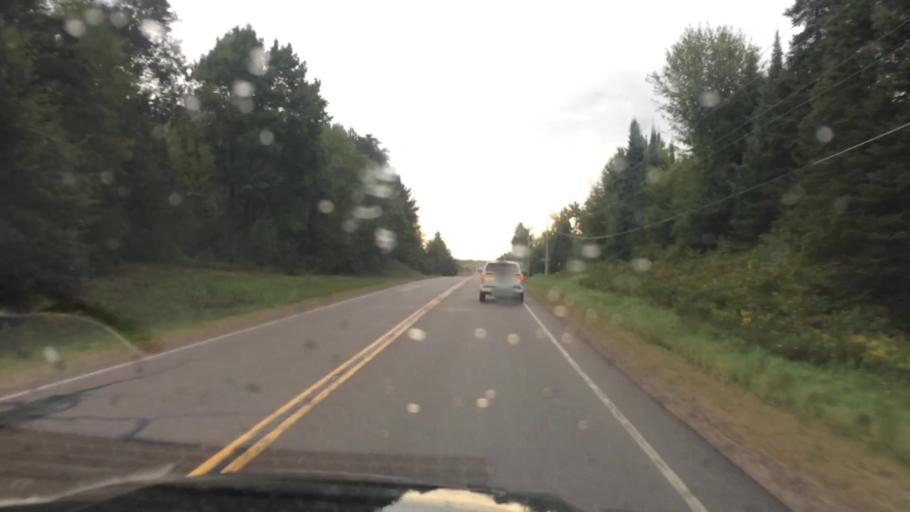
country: US
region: Wisconsin
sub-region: Lincoln County
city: Tomahawk
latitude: 45.4962
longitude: -89.7131
